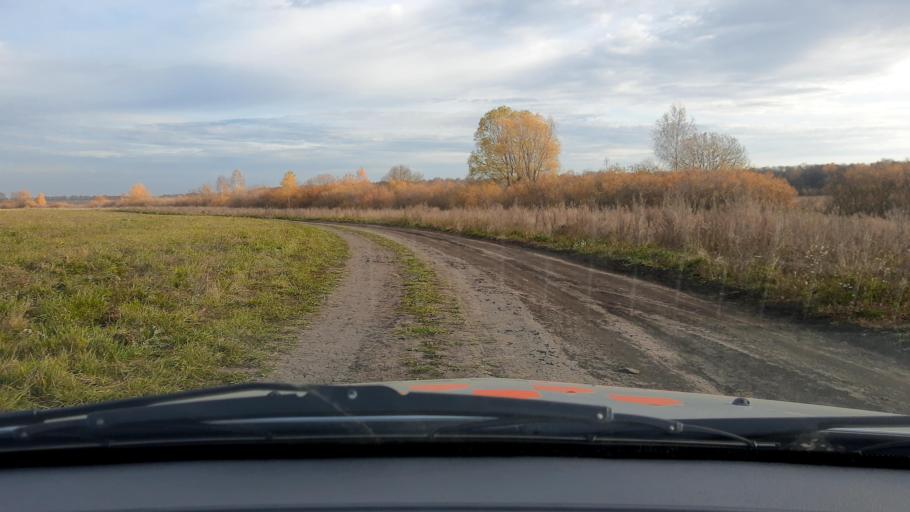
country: RU
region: Bashkortostan
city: Asanovo
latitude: 54.8105
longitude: 55.6117
